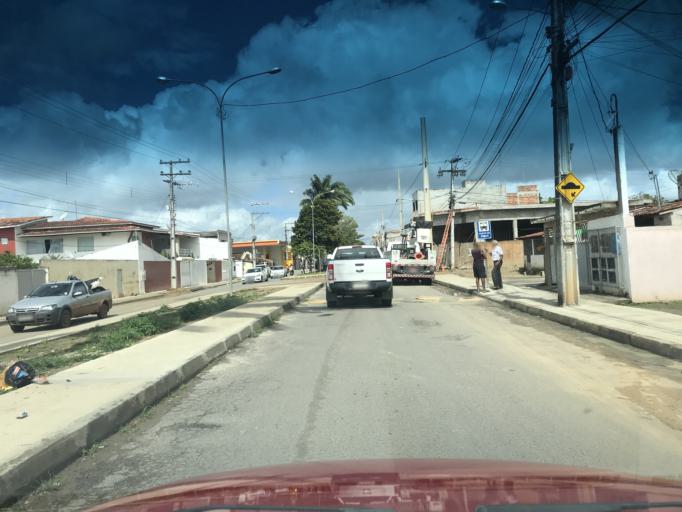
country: BR
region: Bahia
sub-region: Santo Antonio De Jesus
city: Santo Antonio de Jesus
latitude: -12.9743
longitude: -39.2738
